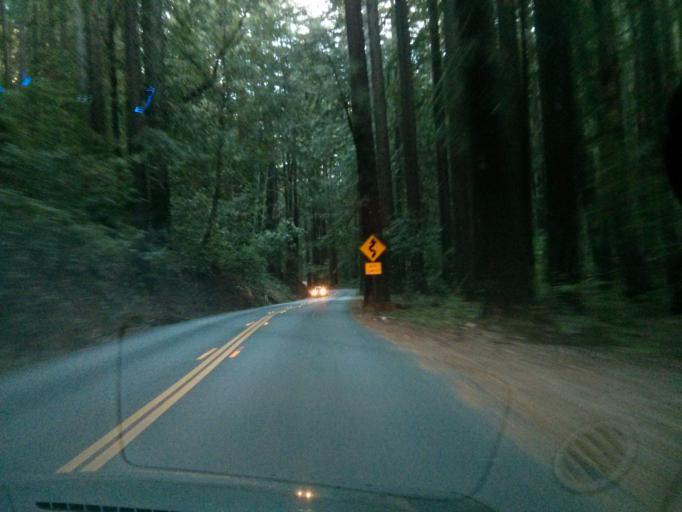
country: US
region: California
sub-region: Santa Cruz County
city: Bonny Doon
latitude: 37.0590
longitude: -122.1163
